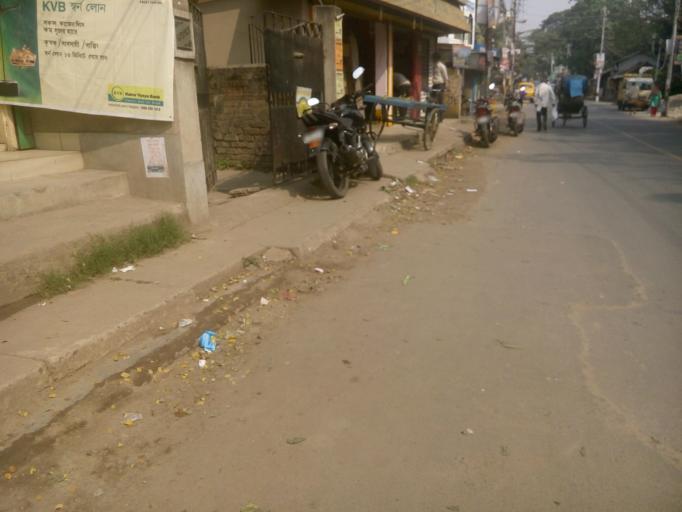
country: IN
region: West Bengal
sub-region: South 24 Paraganas
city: Santoshpur
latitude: 22.4577
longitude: 88.3089
